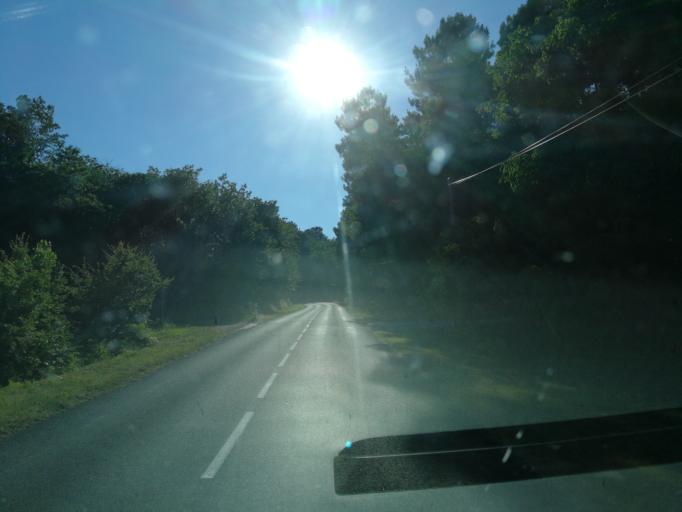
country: FR
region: Midi-Pyrenees
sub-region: Departement du Lot
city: Salviac
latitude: 44.6135
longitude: 1.2075
